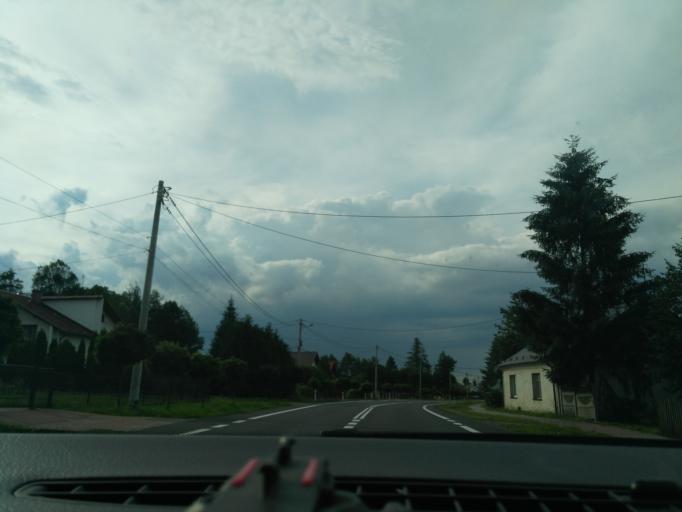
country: PL
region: Subcarpathian Voivodeship
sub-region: Powiat rzeszowski
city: Kamien
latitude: 50.3490
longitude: 22.1273
